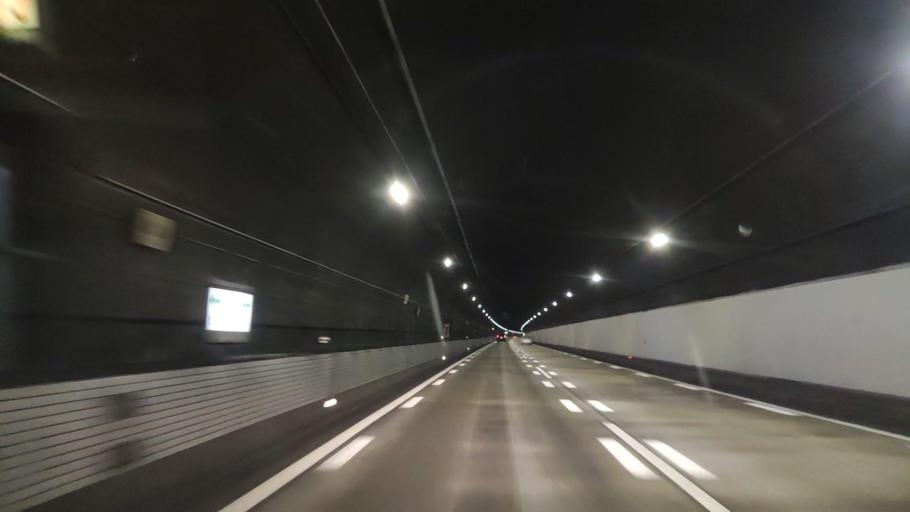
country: JP
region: Hiroshima
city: Fukuyama
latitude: 34.4988
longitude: 133.3204
